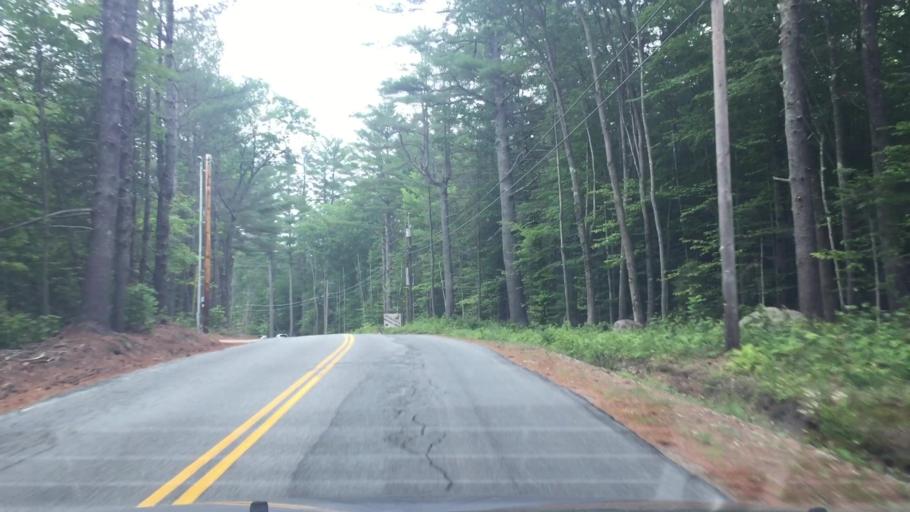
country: US
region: New Hampshire
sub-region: Carroll County
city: North Conway
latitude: 44.0988
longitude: -71.1857
